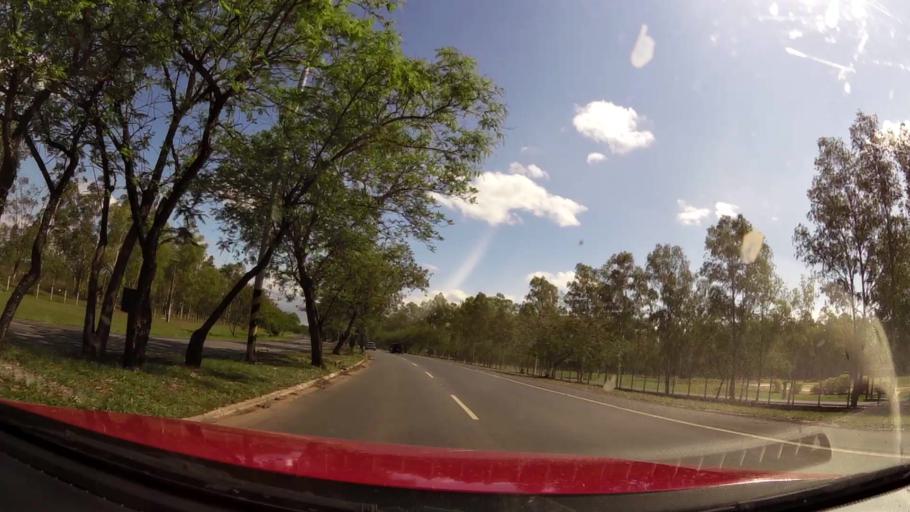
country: PY
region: Central
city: Fernando de la Mora
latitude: -25.2633
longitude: -57.5337
